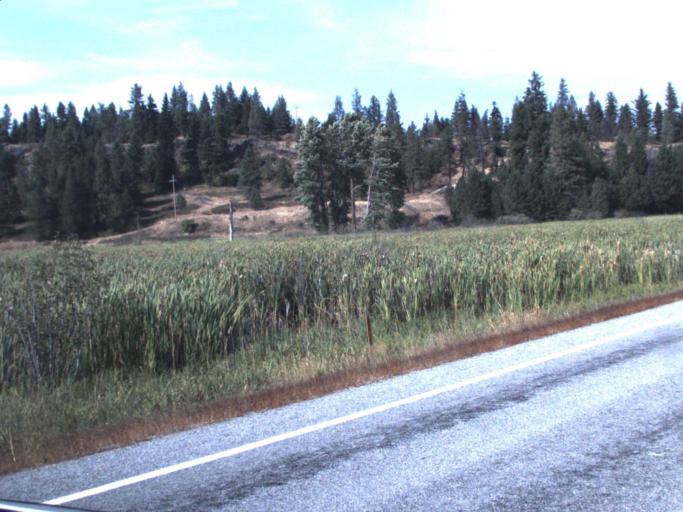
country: US
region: Washington
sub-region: Pend Oreille County
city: Newport
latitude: 48.2333
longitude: -117.2857
